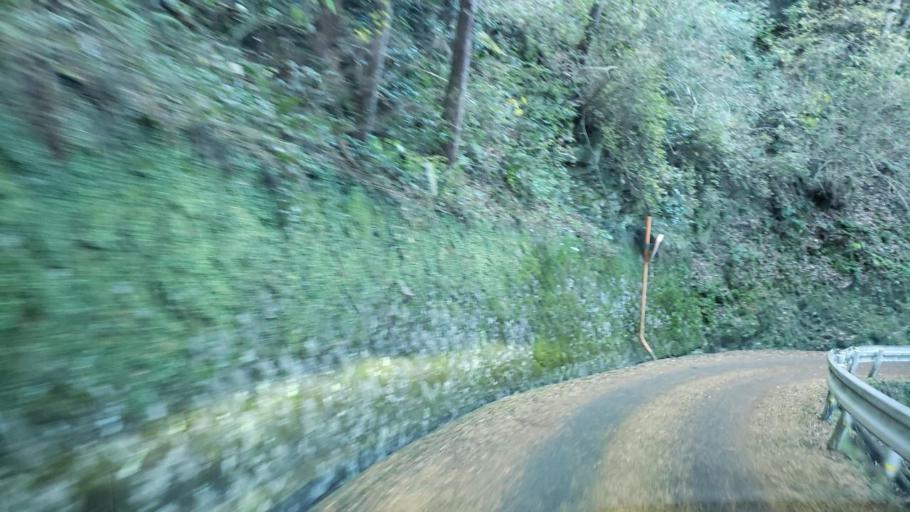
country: JP
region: Tokushima
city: Wakimachi
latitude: 34.0202
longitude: 134.0401
